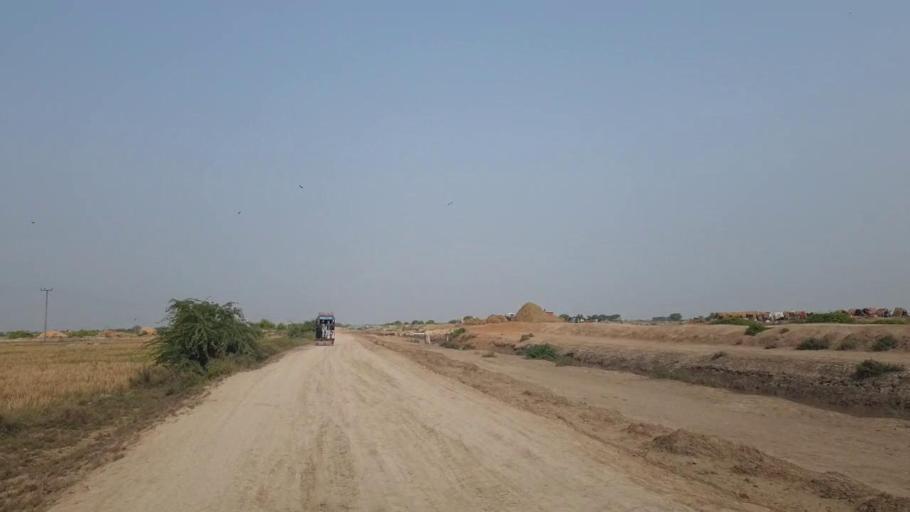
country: PK
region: Sindh
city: Badin
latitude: 24.7101
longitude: 68.7735
